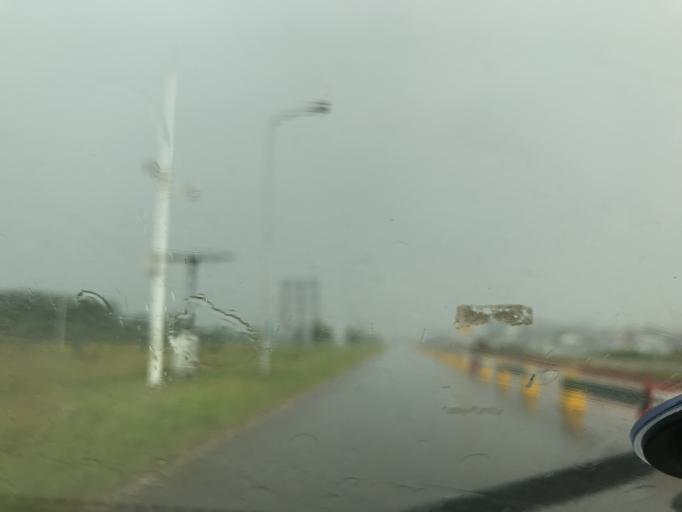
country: NG
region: Lagos
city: Oshodi
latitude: 6.5694
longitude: 3.3214
